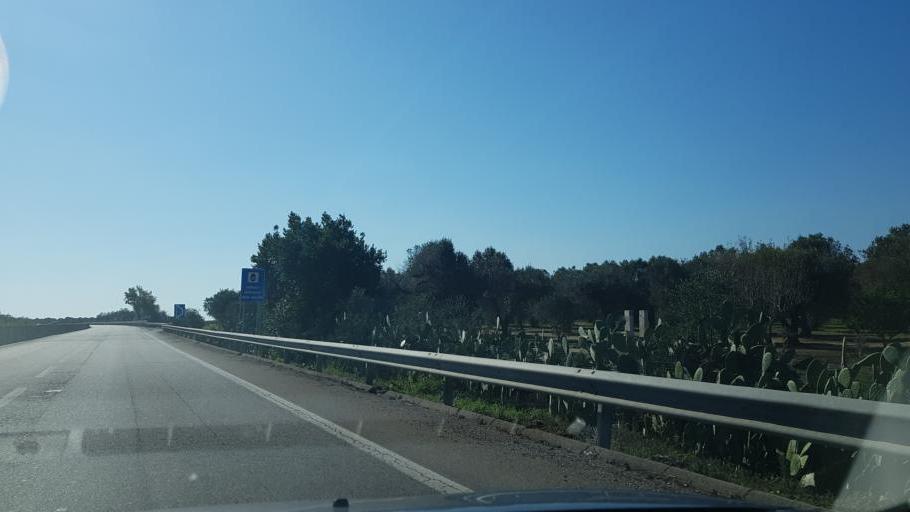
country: IT
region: Apulia
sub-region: Provincia di Brindisi
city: Tuturano
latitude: 40.5441
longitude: 18.0005
